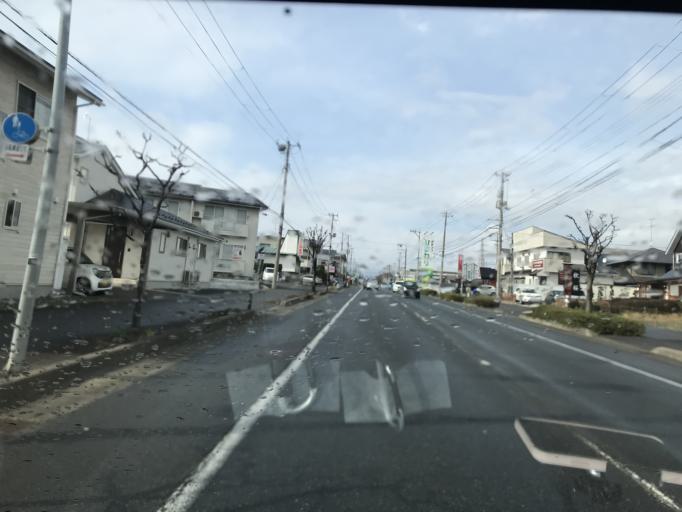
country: JP
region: Iwate
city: Kitakami
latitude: 39.3065
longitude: 141.1152
